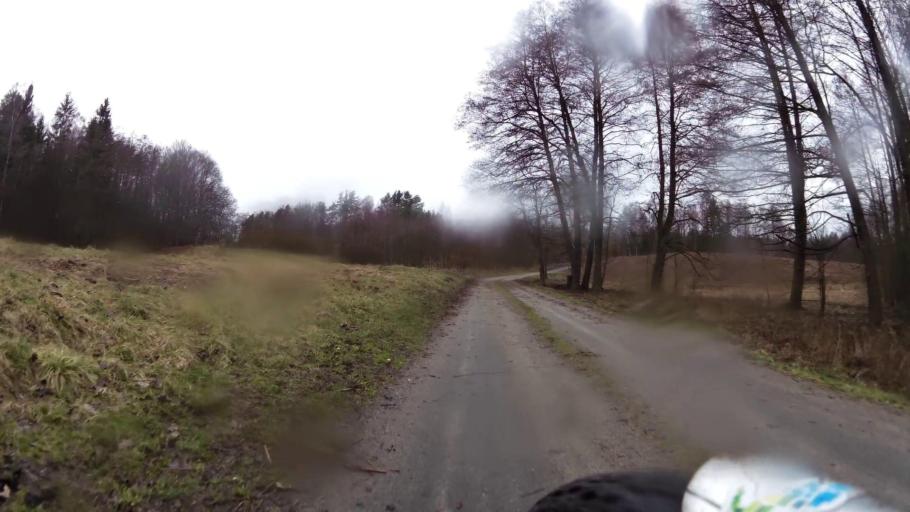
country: PL
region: Pomeranian Voivodeship
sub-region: Powiat bytowski
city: Miastko
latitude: 54.0426
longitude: 17.0526
